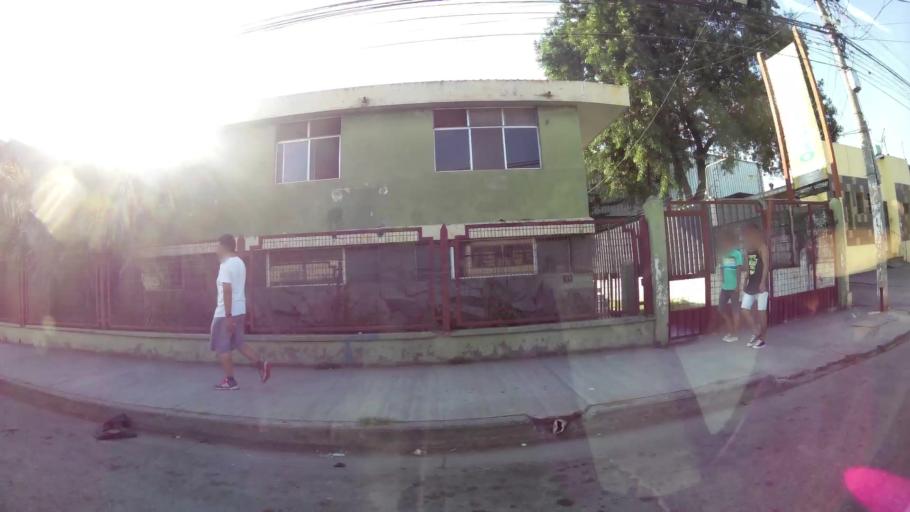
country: EC
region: Guayas
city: Guayaquil
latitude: -2.1562
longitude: -79.9285
